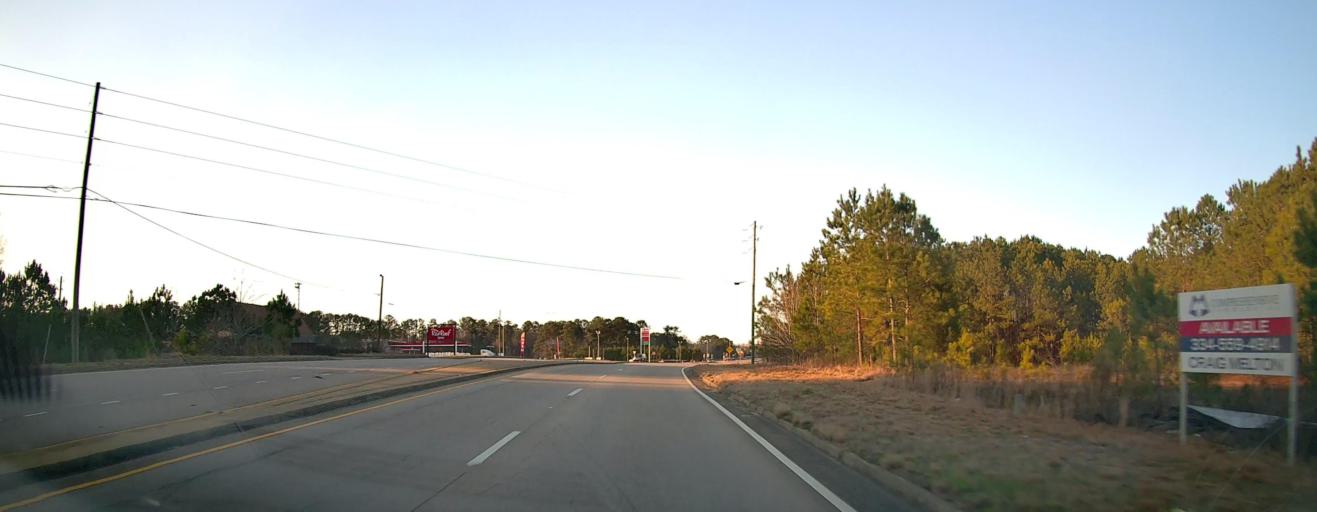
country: US
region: Georgia
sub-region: Troup County
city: La Grange
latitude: 32.9844
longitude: -85.0293
